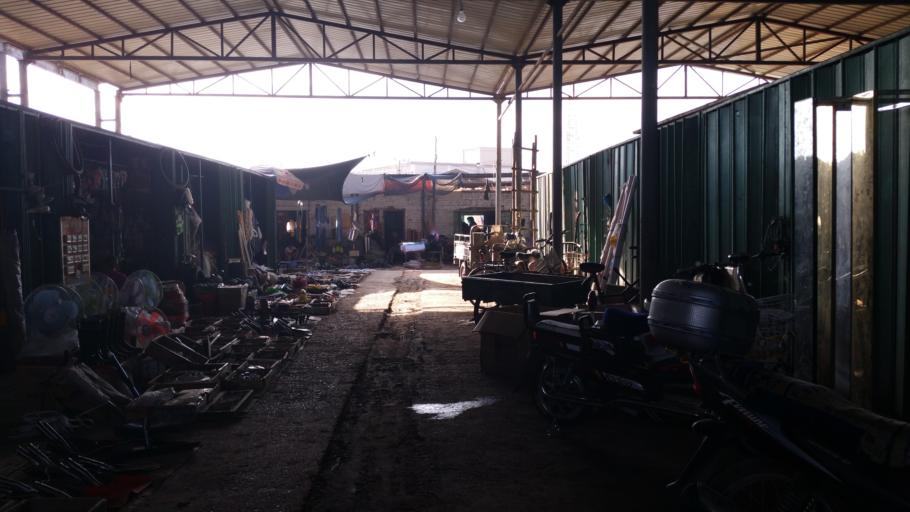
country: CN
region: Xinjiang Uygur Zizhiqu
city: Laochenglu
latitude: 42.9399
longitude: 89.1737
